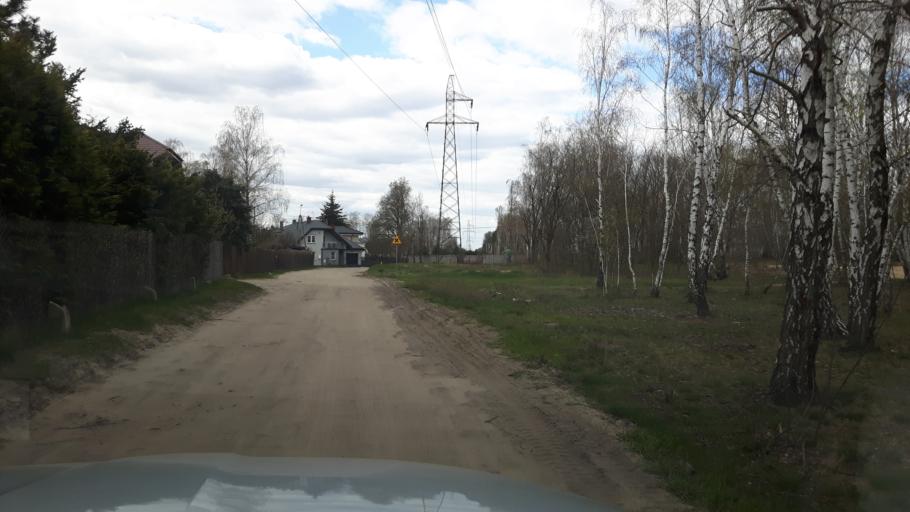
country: PL
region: Masovian Voivodeship
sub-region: Powiat wolominski
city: Kobylka
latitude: 52.3512
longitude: 21.2164
